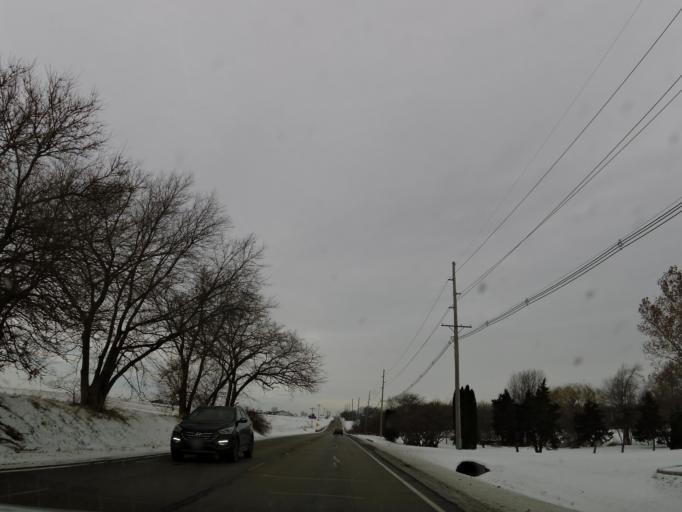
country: US
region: Illinois
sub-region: Putnam County
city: Granville
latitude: 41.2575
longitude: -89.2314
